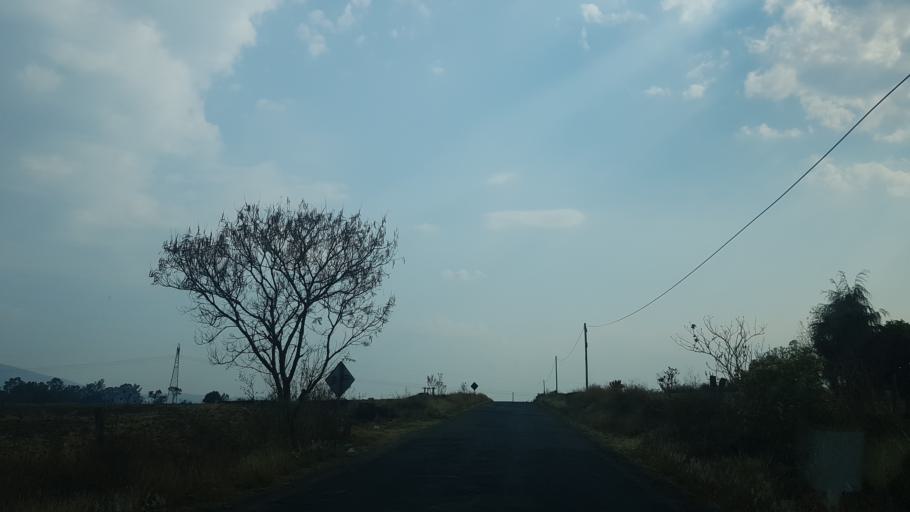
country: MX
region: Puebla
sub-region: Santa Isabel Cholula
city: Santa Ana Acozautla
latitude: 18.9559
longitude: -98.3936
